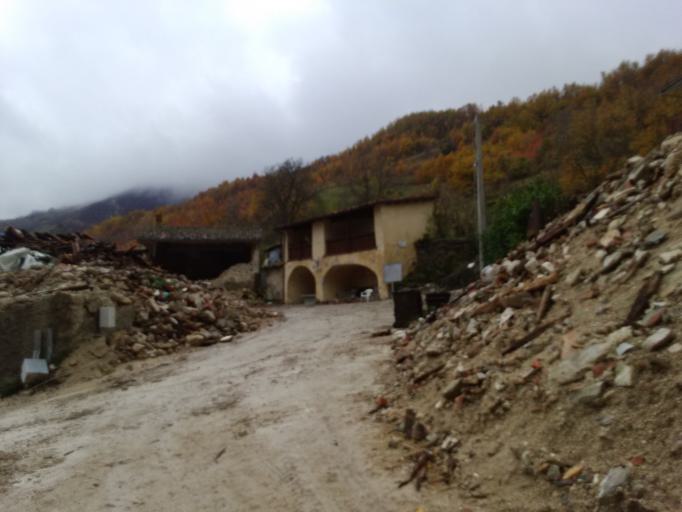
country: IT
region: Latium
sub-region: Provincia di Rieti
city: Accumoli
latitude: 42.6935
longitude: 13.2075
